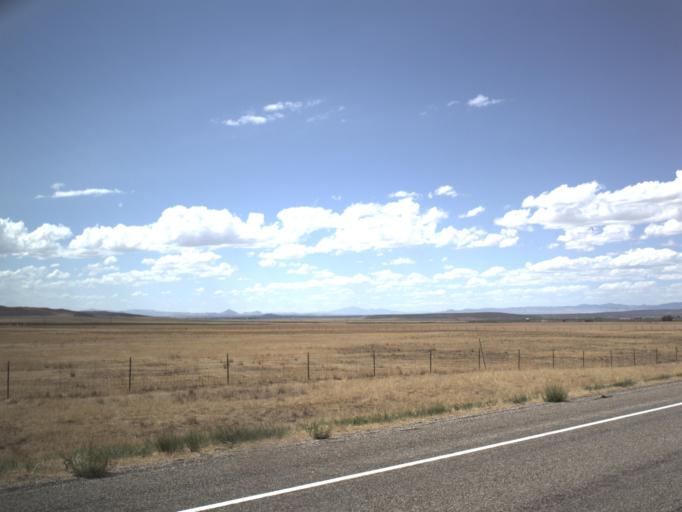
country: US
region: Utah
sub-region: Millard County
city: Fillmore
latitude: 39.1144
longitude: -112.2902
